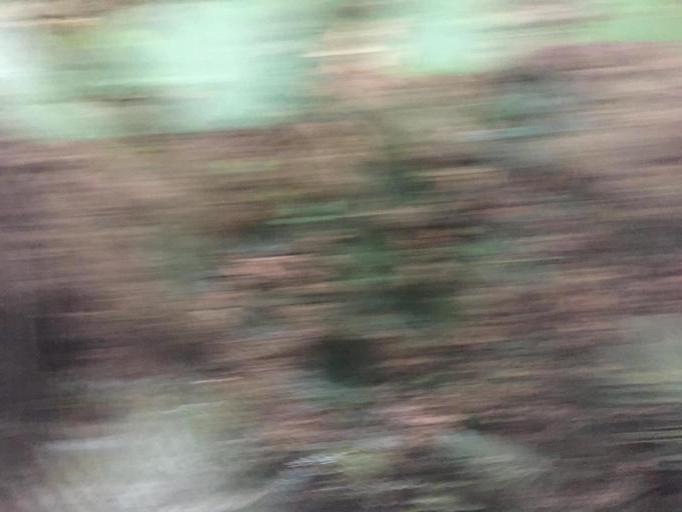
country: TW
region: Taiwan
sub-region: Chiayi
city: Jiayi Shi
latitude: 23.5406
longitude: 120.6063
